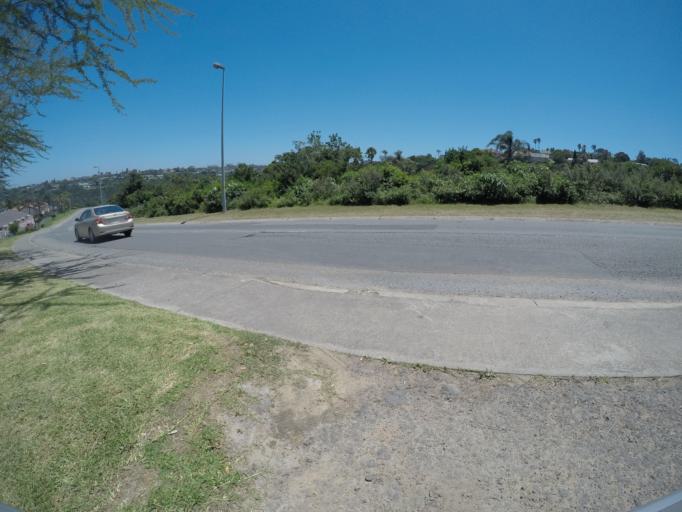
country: ZA
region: Eastern Cape
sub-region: Buffalo City Metropolitan Municipality
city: East London
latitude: -32.9796
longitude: 27.9392
